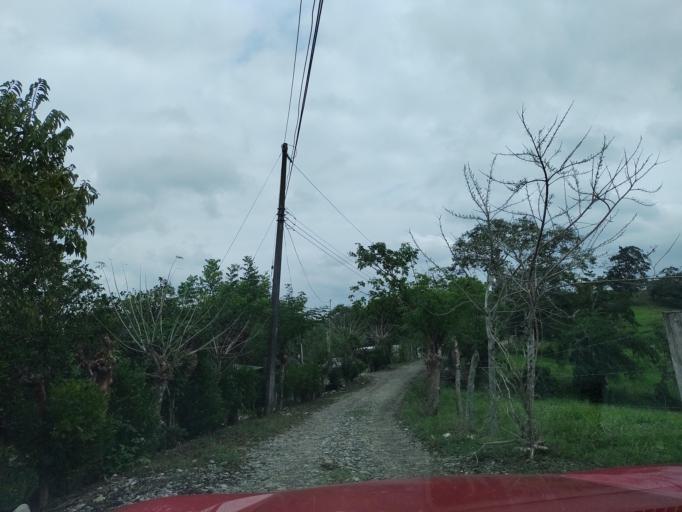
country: MX
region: Veracruz
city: Coatzintla
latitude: 20.4574
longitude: -97.4139
